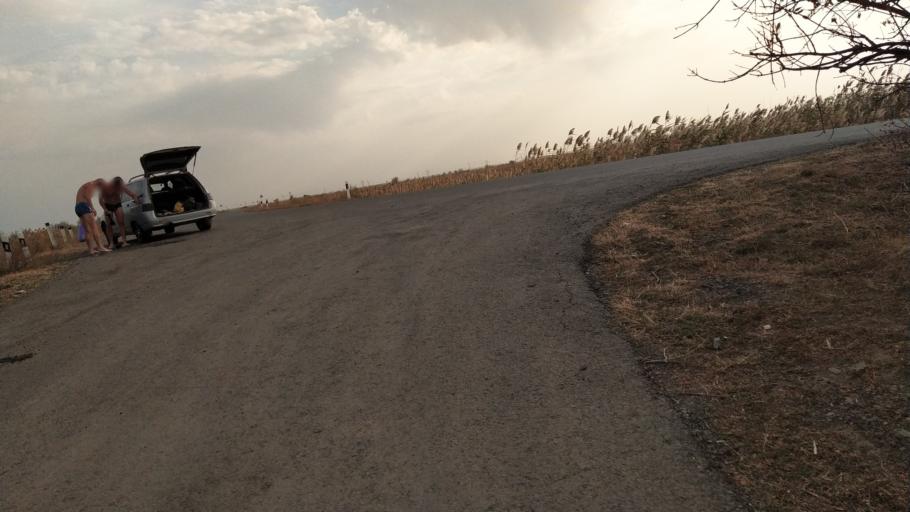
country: RU
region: Rostov
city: Kuleshovka
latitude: 47.1345
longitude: 39.5807
